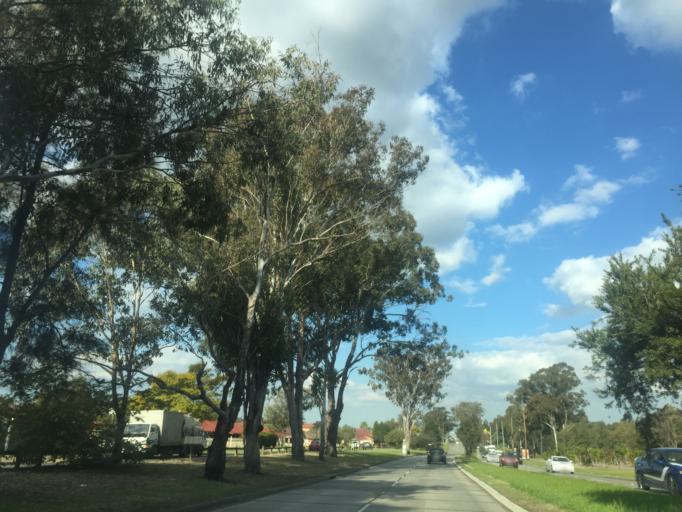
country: AU
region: New South Wales
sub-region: Blacktown
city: Quakers Hill
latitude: -33.7452
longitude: 150.8767
